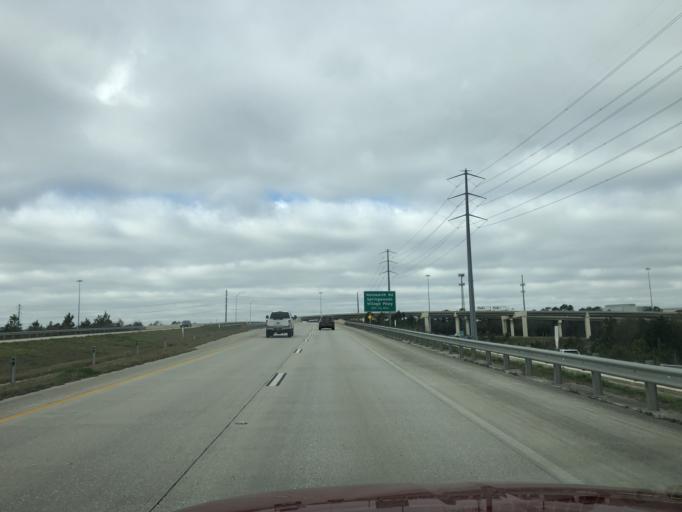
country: US
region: Texas
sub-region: Harris County
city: Spring
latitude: 30.0928
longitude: -95.4319
